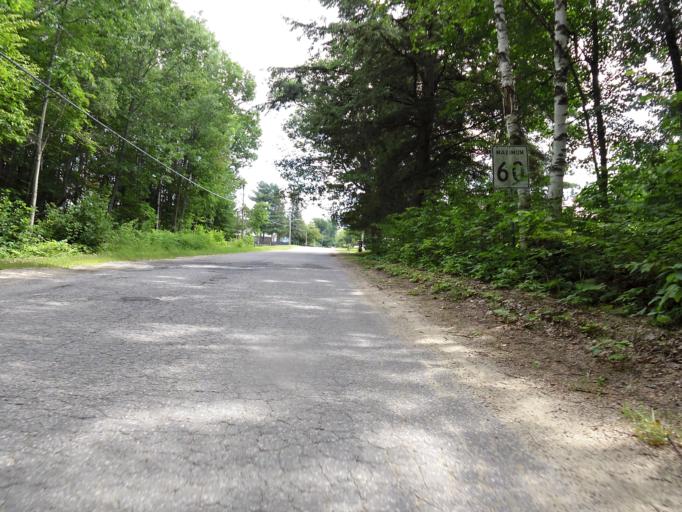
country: CA
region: Quebec
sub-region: Outaouais
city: Wakefield
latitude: 45.8121
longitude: -76.0264
